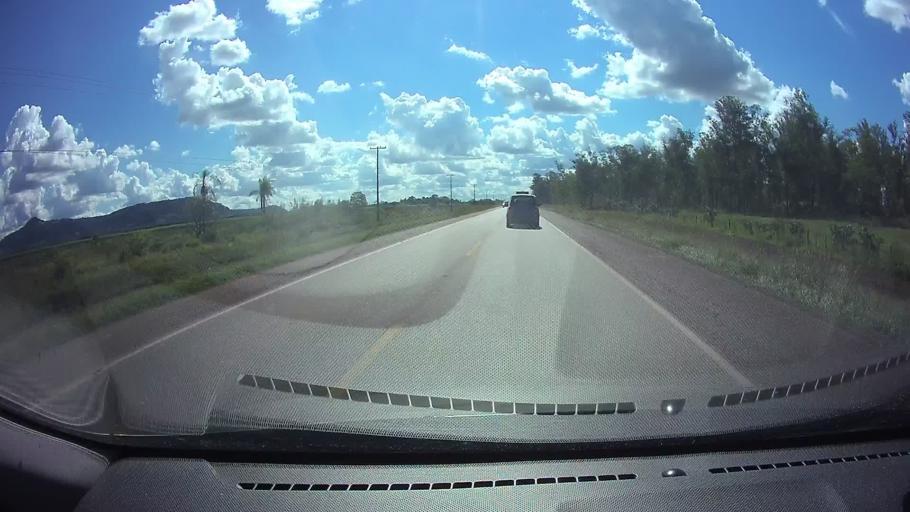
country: PY
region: Paraguari
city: La Colmena
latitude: -25.7553
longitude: -56.7684
